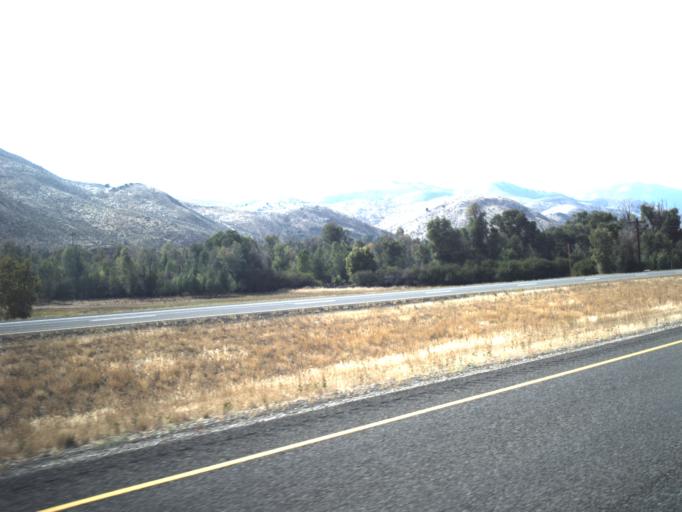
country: US
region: Utah
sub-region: Summit County
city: Coalville
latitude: 40.9923
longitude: -111.4588
